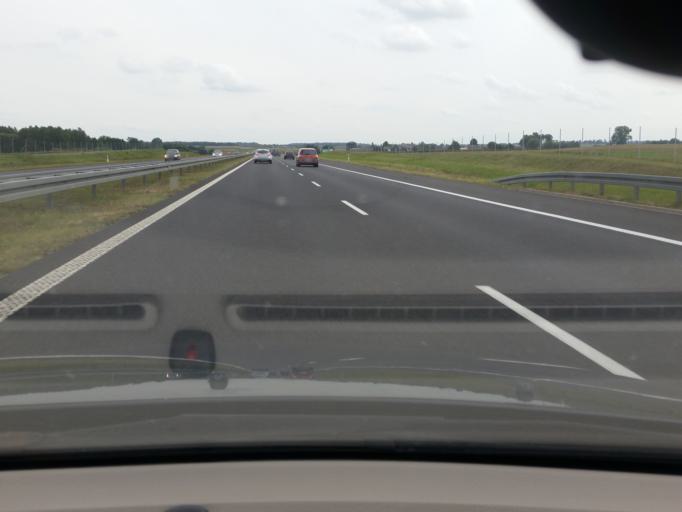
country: PL
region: Pomeranian Voivodeship
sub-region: Powiat starogardzki
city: Smetowo Graniczne
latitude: 53.7778
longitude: 18.6307
